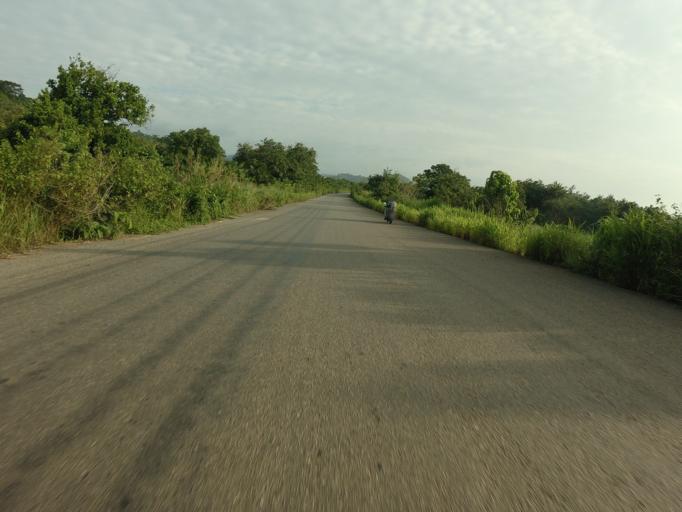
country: GH
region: Volta
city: Kpandu
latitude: 6.9094
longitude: 0.4458
